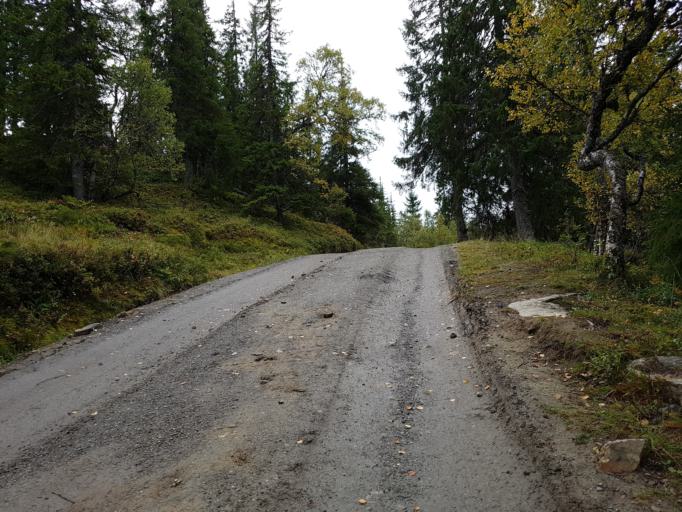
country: NO
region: Sor-Trondelag
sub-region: Melhus
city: Melhus
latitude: 63.4144
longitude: 10.2554
